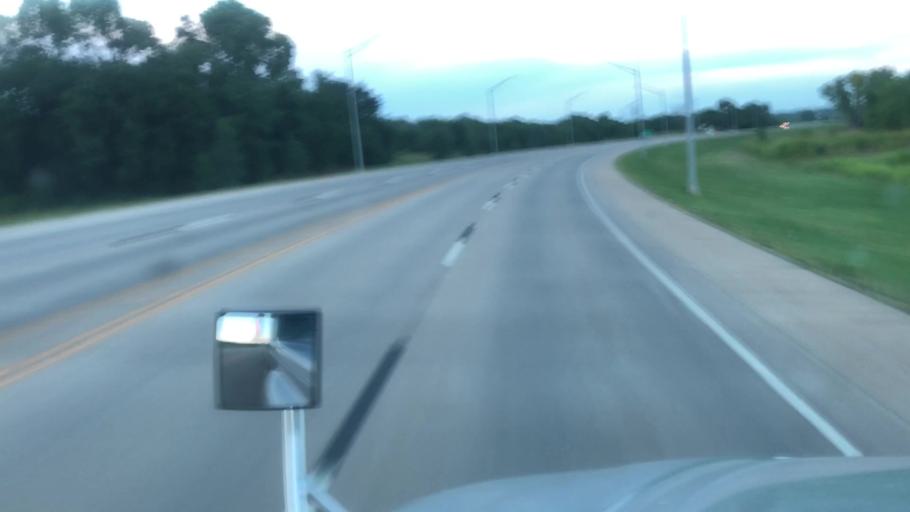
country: US
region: Oklahoma
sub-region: Kay County
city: Ponca City
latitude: 36.6836
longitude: -97.0700
